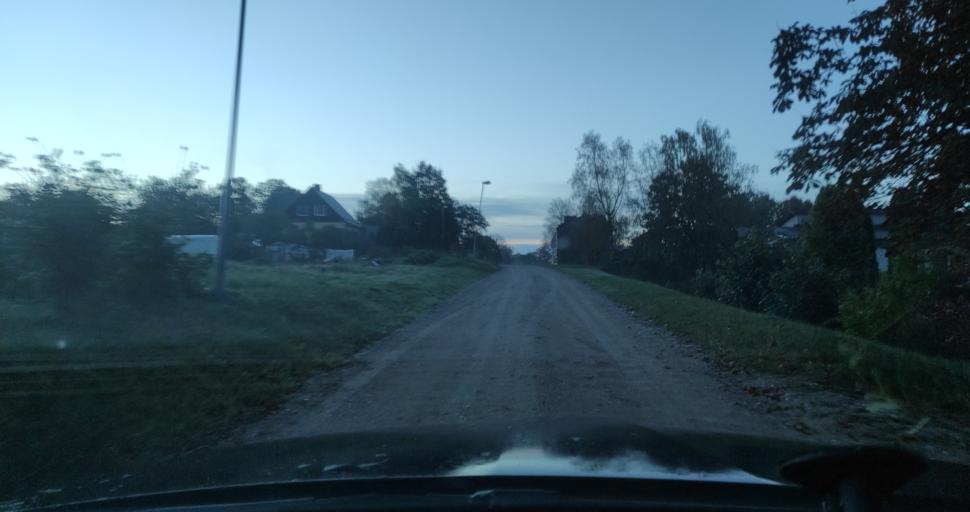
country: LV
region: Kuldigas Rajons
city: Kuldiga
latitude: 56.8839
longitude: 21.8188
